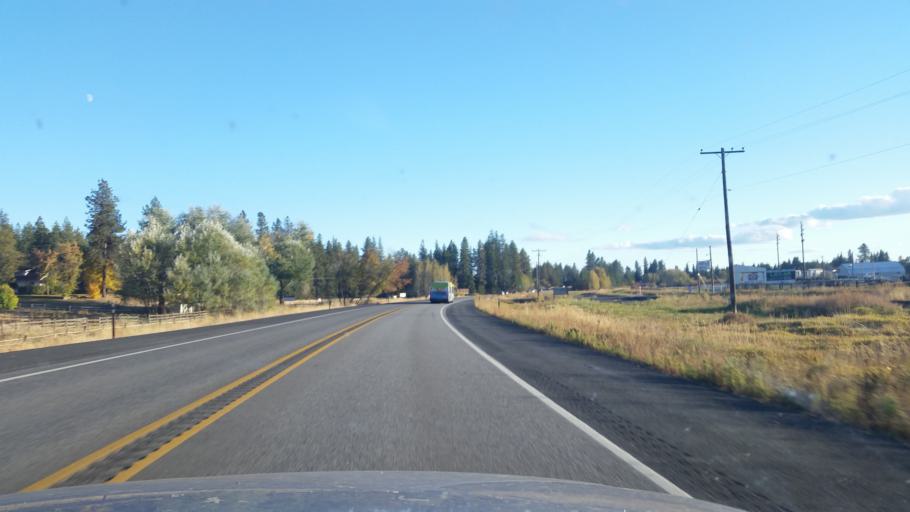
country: US
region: Washington
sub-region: Spokane County
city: Cheney
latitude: 47.5271
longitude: -117.5673
